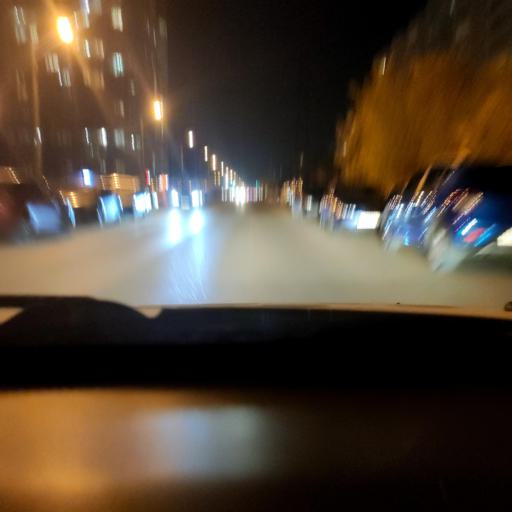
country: RU
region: Perm
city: Kondratovo
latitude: 57.9693
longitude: 56.1680
